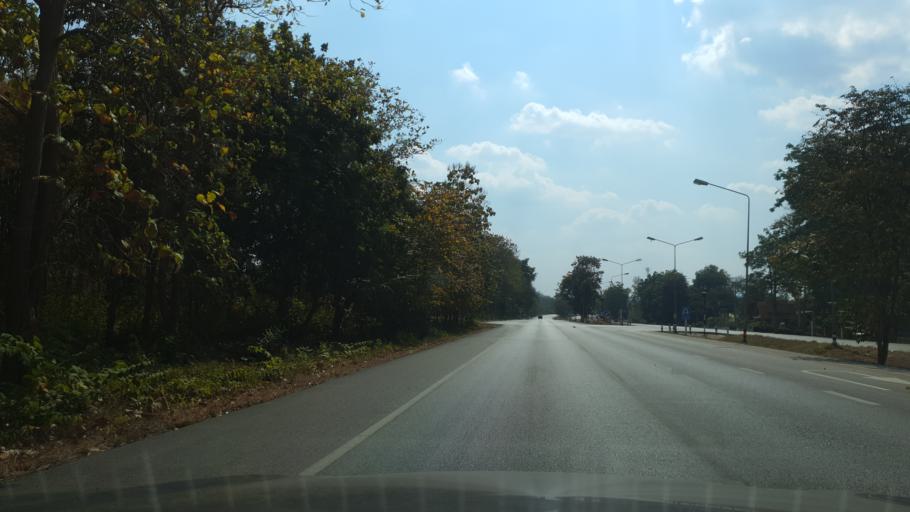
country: TH
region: Lampang
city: Mae Phrik
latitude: 17.4041
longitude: 99.1495
